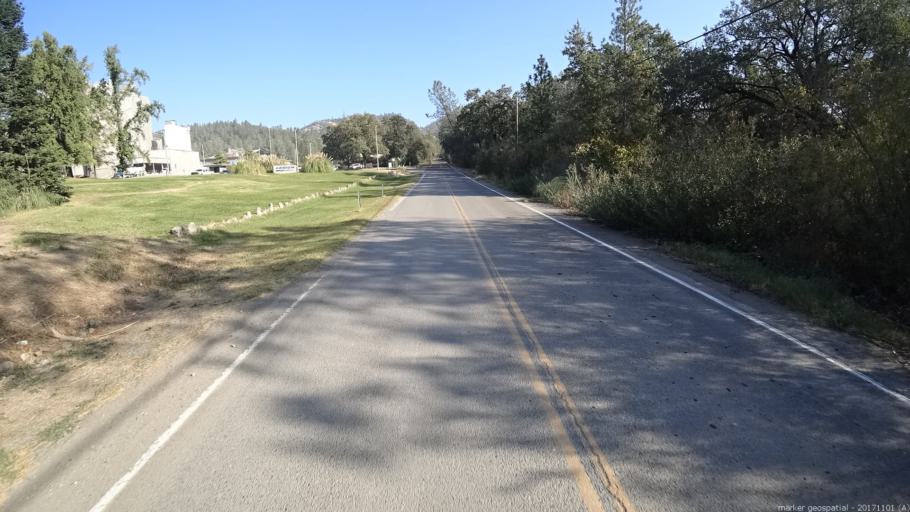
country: US
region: California
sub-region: Shasta County
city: Shasta Lake
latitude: 40.7340
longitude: -122.3216
